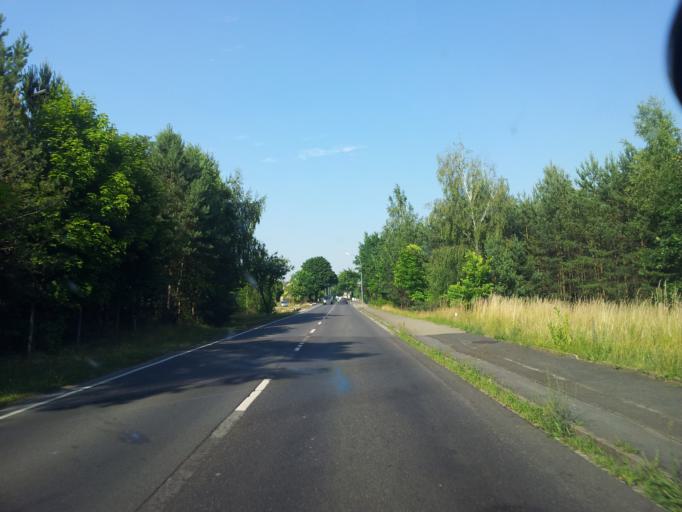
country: DE
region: Saxony
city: Schwepnitz
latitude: 51.3256
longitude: 13.9498
